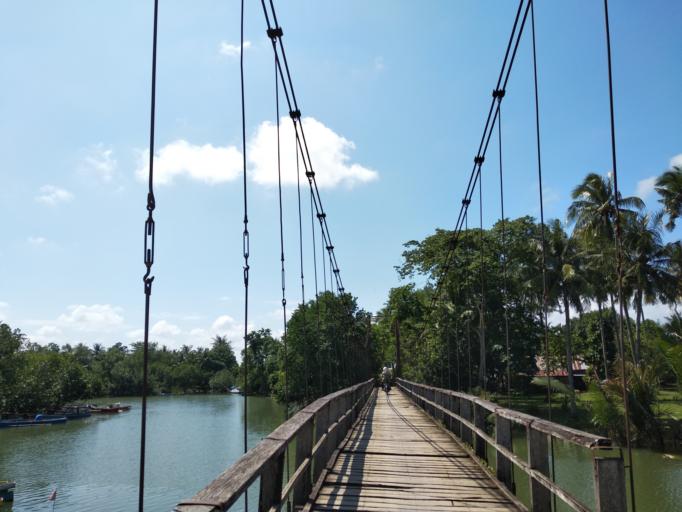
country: ID
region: South Sulawesi
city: Kadai
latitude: -4.7400
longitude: 120.3869
